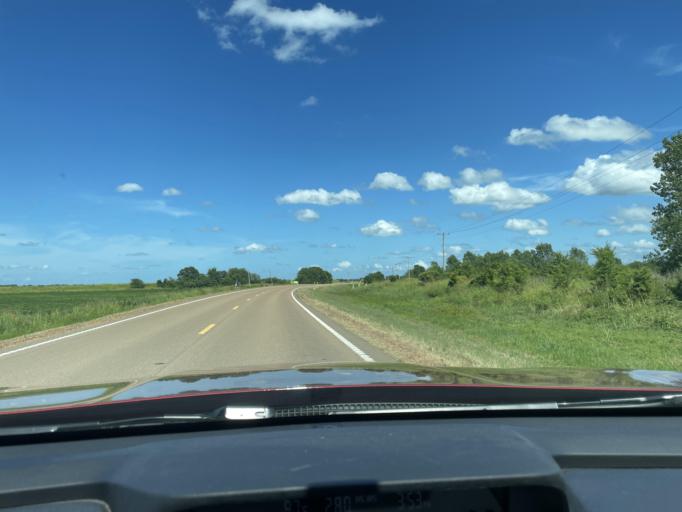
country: US
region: Mississippi
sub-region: Humphreys County
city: Belzoni
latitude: 33.1843
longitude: -90.6638
